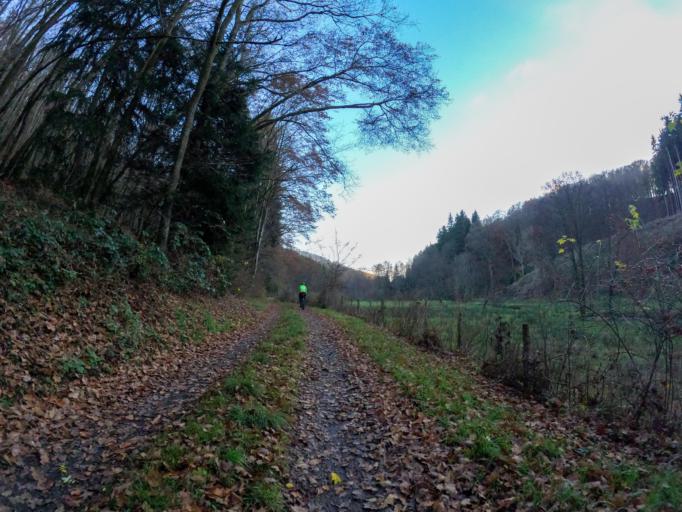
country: LU
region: Diekirch
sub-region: Canton de Wiltz
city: Bavigne
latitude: 49.9366
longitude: 5.8405
